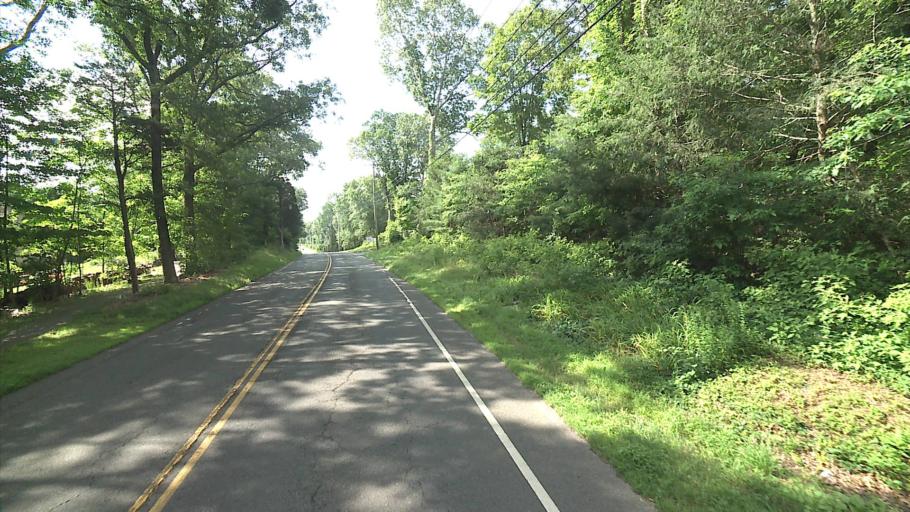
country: US
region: Connecticut
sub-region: Middlesex County
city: Clinton
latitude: 41.2991
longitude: -72.4912
